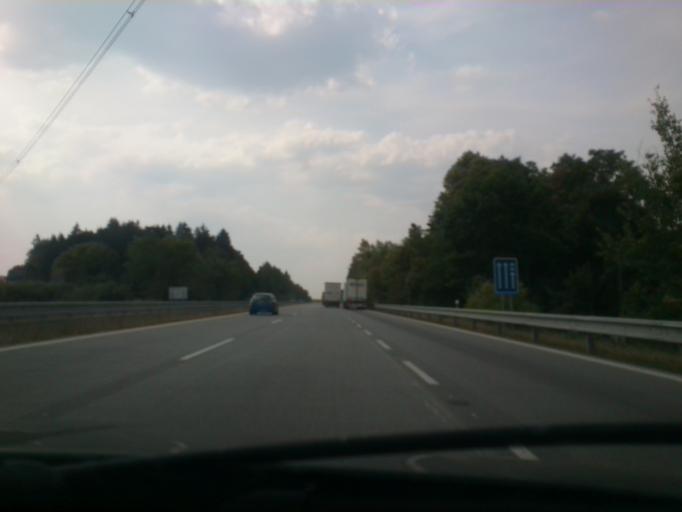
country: CZ
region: Central Bohemia
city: Divisov
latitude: 49.7978
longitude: 14.9179
